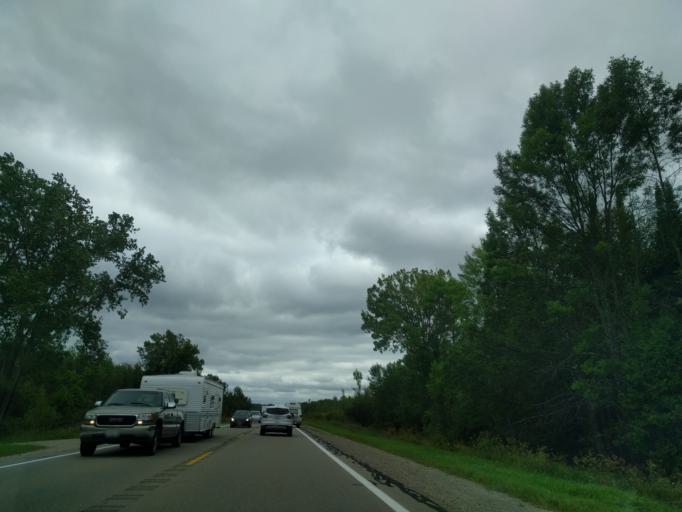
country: US
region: Michigan
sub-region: Menominee County
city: Menominee
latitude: 45.3387
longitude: -87.4162
